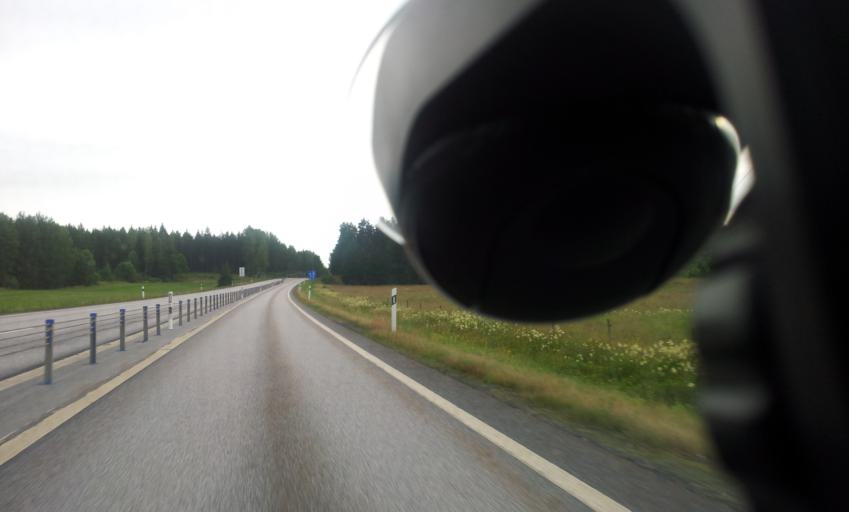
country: SE
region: OEstergoetland
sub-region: Valdemarsviks Kommun
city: Valdemarsvik
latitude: 58.1239
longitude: 16.5342
